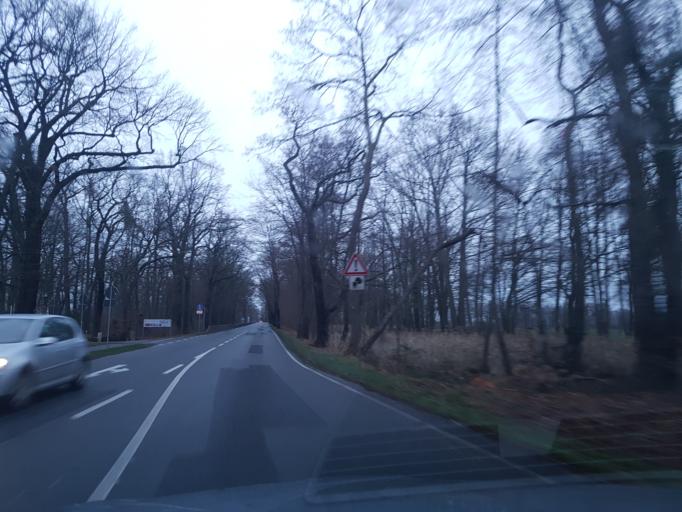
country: DE
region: Brandenburg
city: Elsterwerda
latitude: 51.4475
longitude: 13.5160
